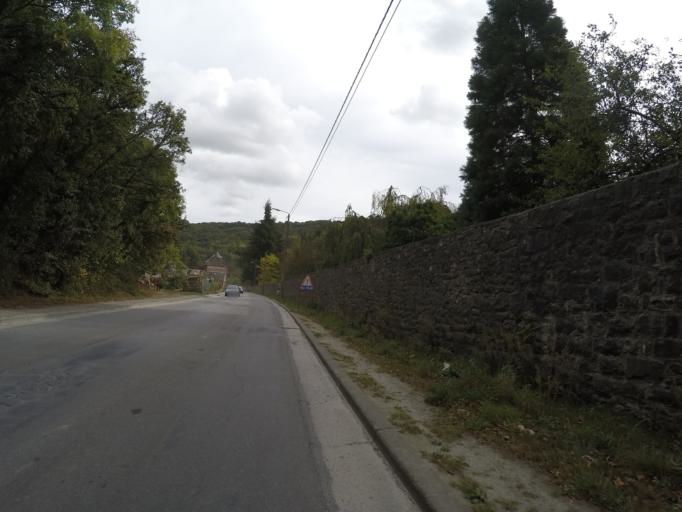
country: BE
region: Wallonia
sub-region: Province de Namur
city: Yvoir
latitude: 50.3270
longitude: 4.8875
